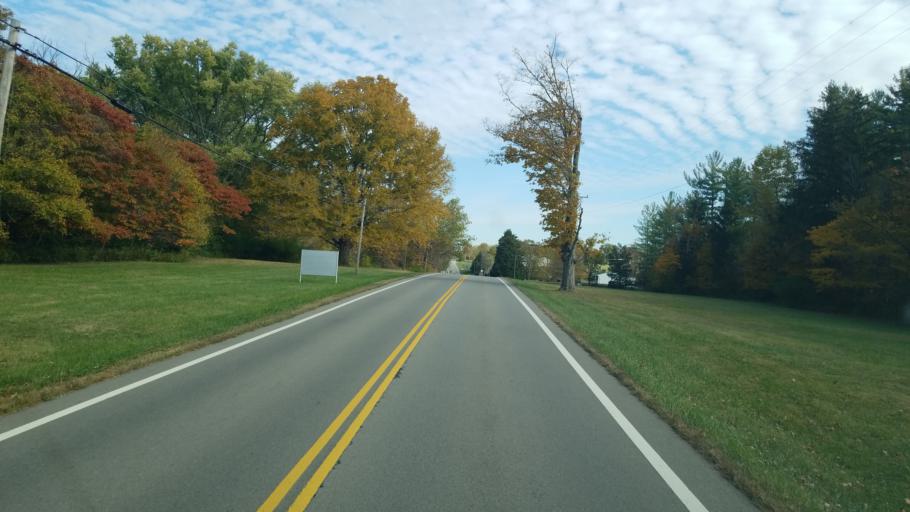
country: US
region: Ohio
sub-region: Warren County
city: Morrow
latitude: 39.4083
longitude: -84.0856
